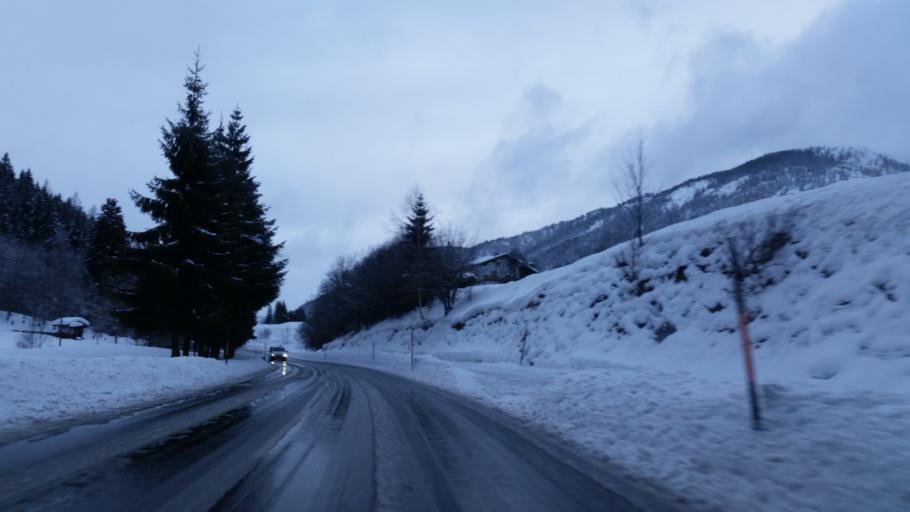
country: AT
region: Salzburg
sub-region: Politischer Bezirk Zell am See
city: Leogang
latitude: 47.4461
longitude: 12.6922
